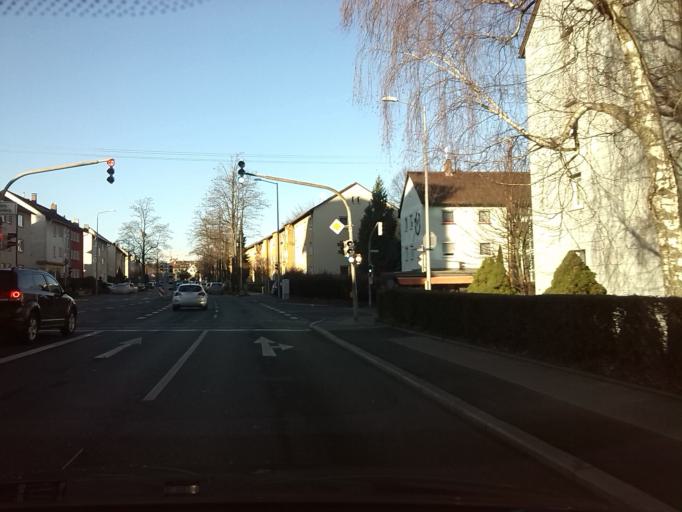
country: DE
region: Baden-Wuerttemberg
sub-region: Regierungsbezirk Stuttgart
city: Ludwigsburg
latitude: 48.8893
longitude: 9.2092
